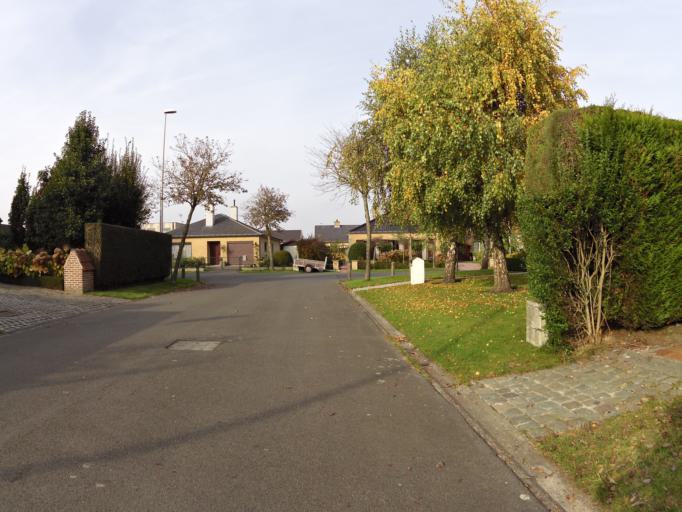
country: BE
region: Flanders
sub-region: Provincie West-Vlaanderen
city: Gistel
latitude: 51.1561
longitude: 2.9790
